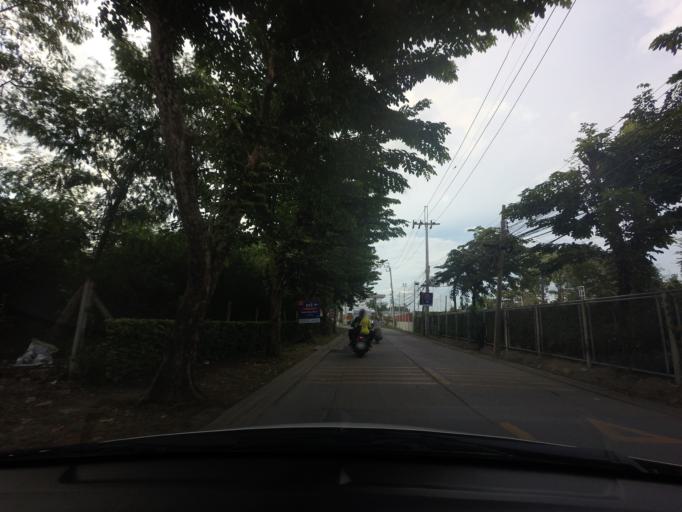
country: TH
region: Bangkok
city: Lak Si
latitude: 13.8965
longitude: 100.5783
